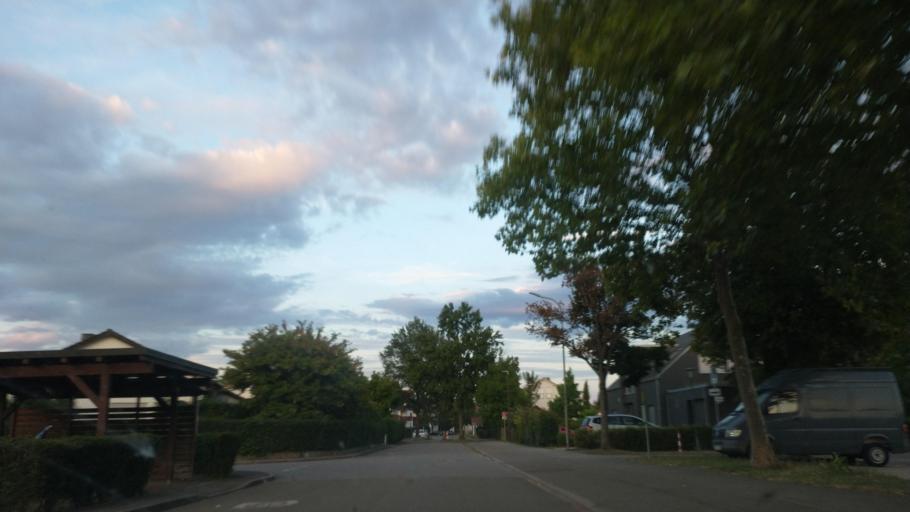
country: DE
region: Baden-Wuerttemberg
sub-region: Freiburg Region
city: Willstatt
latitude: 48.5391
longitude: 7.8975
